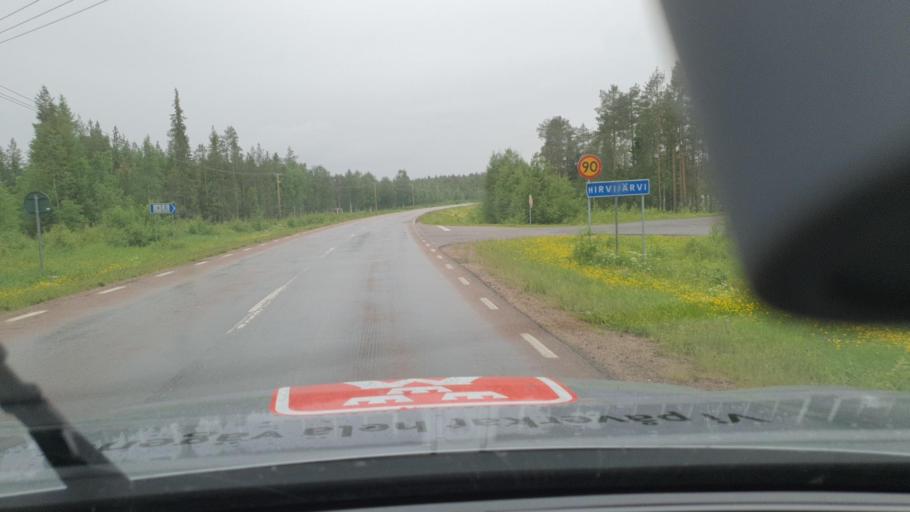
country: SE
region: Norrbotten
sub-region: Overkalix Kommun
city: OEverkalix
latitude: 66.4398
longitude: 23.2204
